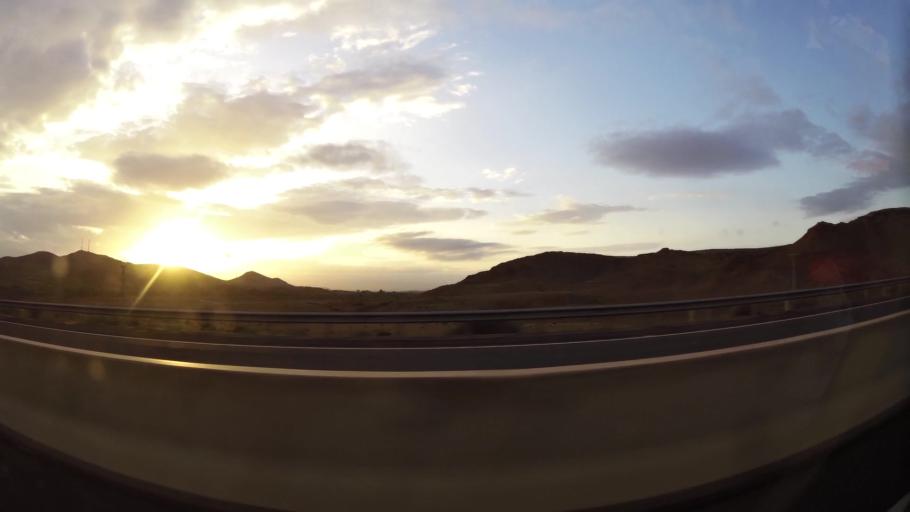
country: MA
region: Oriental
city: Taourirt
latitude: 34.4863
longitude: -2.9808
